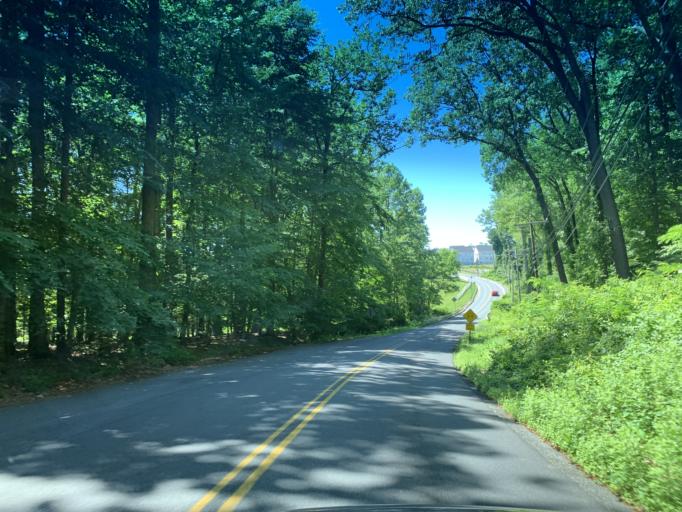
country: US
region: Maryland
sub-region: Harford County
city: Havre de Grace
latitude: 39.5529
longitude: -76.1221
